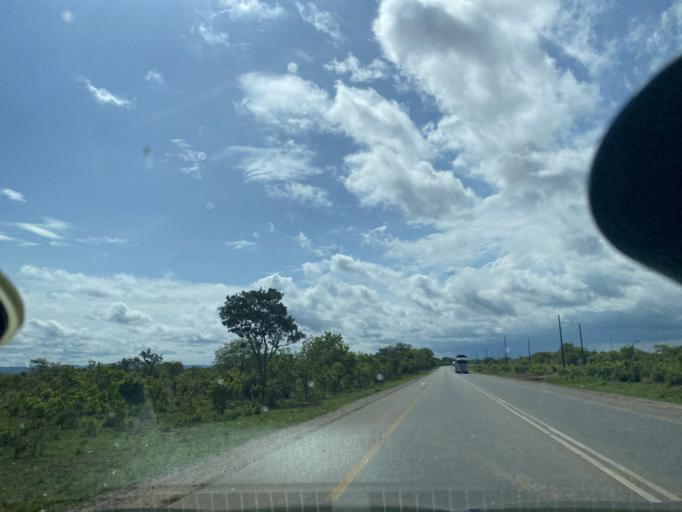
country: ZM
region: Lusaka
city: Kafue
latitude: -15.8586
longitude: 28.2652
